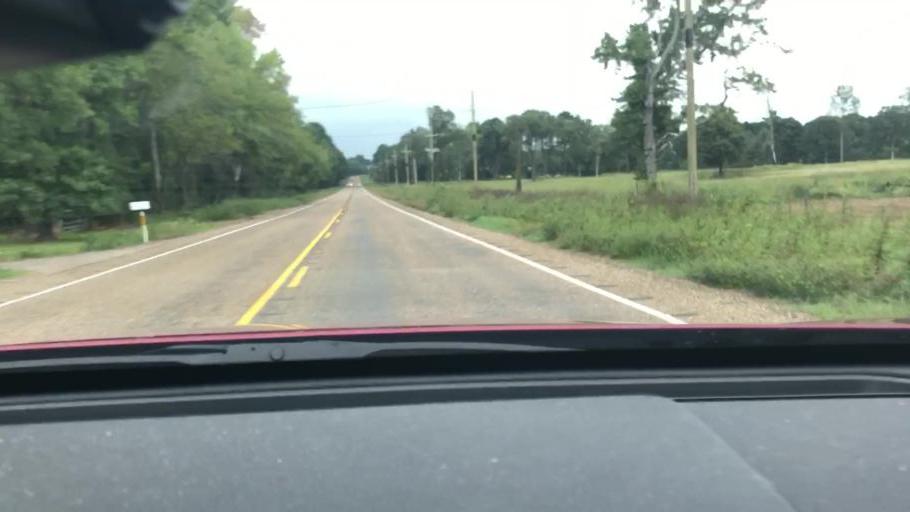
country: US
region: Texas
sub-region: Bowie County
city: Wake Village
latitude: 33.3761
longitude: -94.0997
